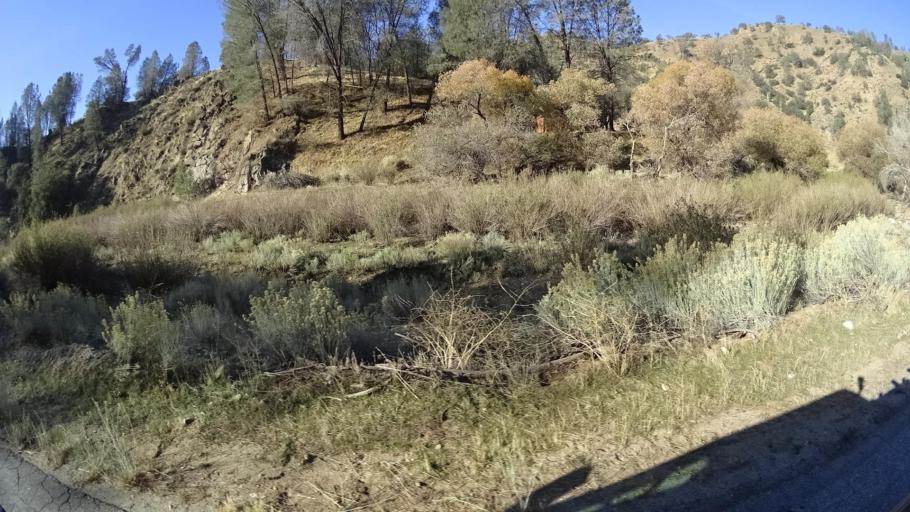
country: US
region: California
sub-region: Kern County
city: Golden Hills
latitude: 35.3055
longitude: -118.4508
